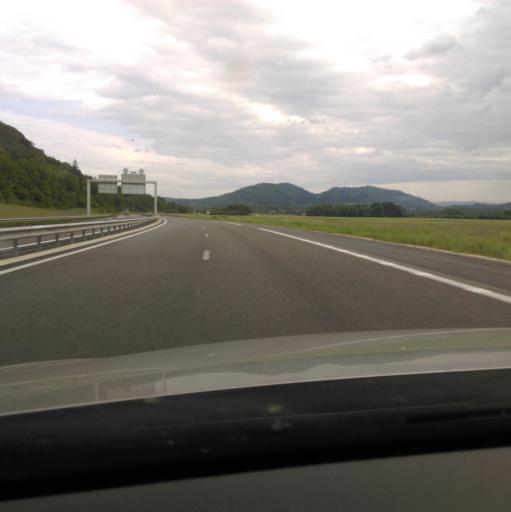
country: FR
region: Rhone-Alpes
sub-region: Departement de l'Ain
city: Saint-Martin-du-Frene
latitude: 46.1494
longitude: 5.5464
